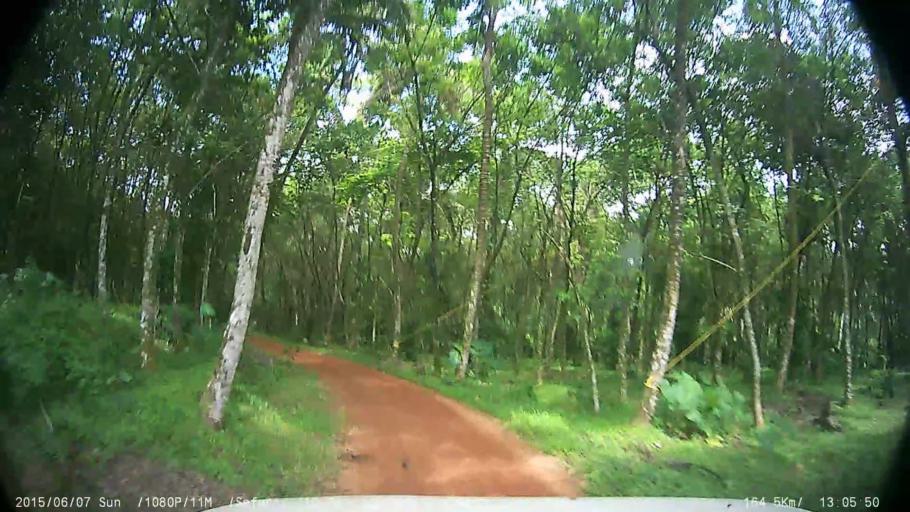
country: IN
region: Kerala
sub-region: Ernakulam
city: Muvattupuzha
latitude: 9.9289
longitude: 76.5707
